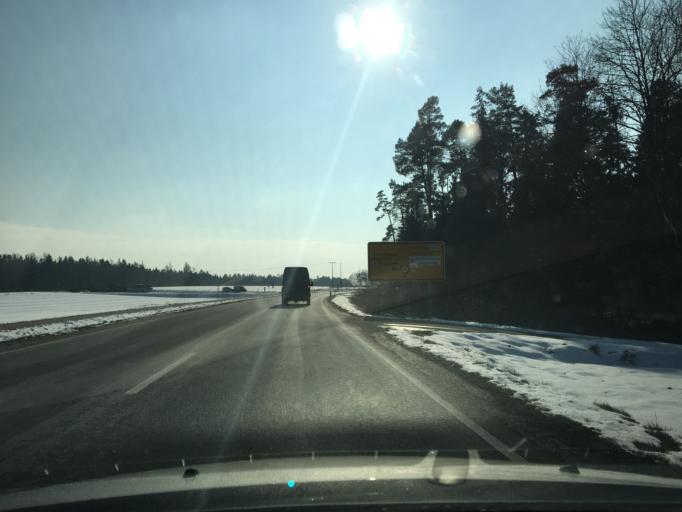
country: DE
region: Bavaria
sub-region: Lower Bavaria
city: Frontenhausen
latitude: 48.5752
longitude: 12.5116
